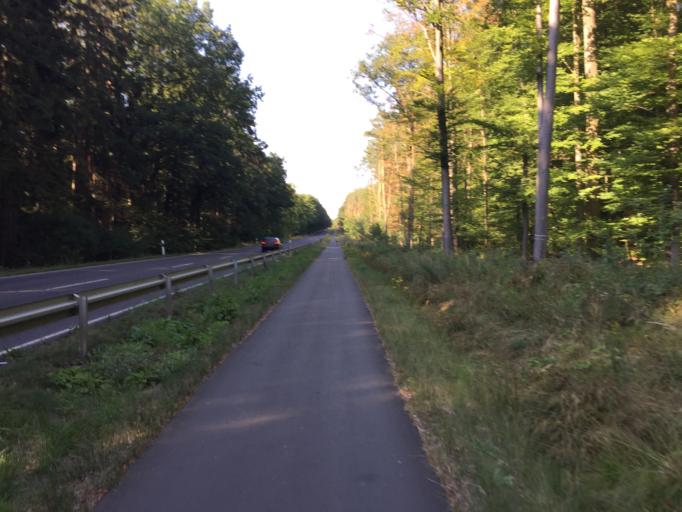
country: DE
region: Hesse
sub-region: Regierungsbezirk Giessen
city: Giessen
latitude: 50.5458
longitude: 8.6767
